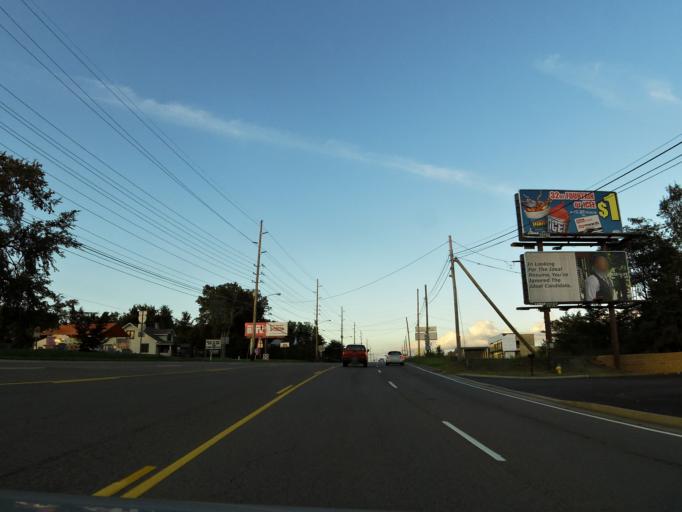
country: US
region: Tennessee
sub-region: Knox County
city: Farragut
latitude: 35.8958
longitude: -84.1369
